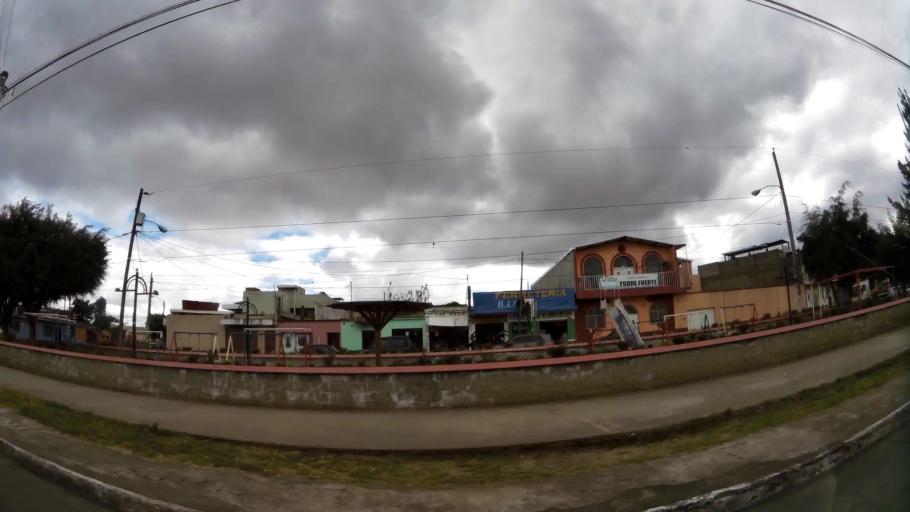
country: GT
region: Guatemala
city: Mixco
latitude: 14.6503
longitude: -90.5782
